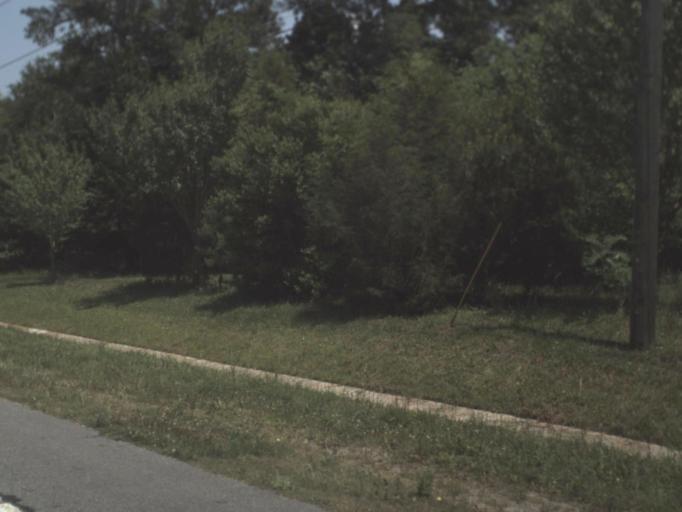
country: US
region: Florida
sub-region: Duval County
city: Baldwin
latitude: 30.2295
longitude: -81.9206
